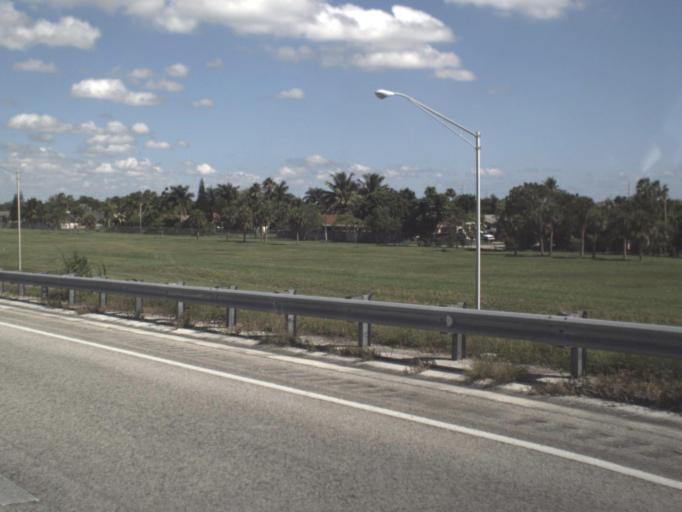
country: US
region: Florida
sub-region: Miami-Dade County
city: Leisure City
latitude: 25.5014
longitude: -80.4171
